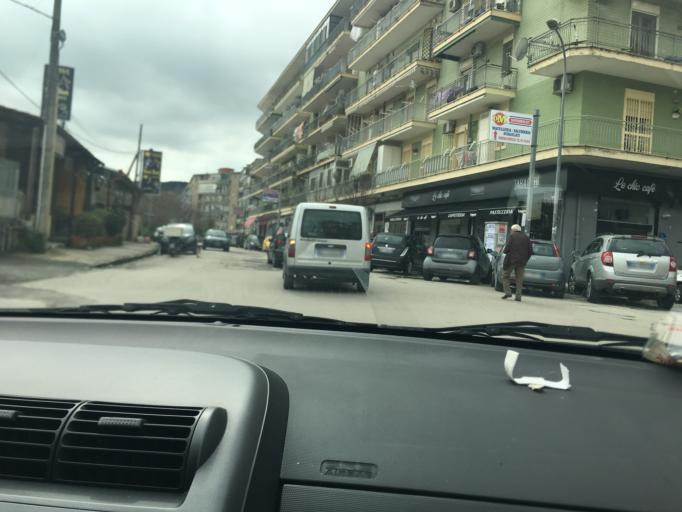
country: IT
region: Campania
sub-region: Provincia di Napoli
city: Mugnano di Napoli
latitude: 40.8972
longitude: 14.2041
